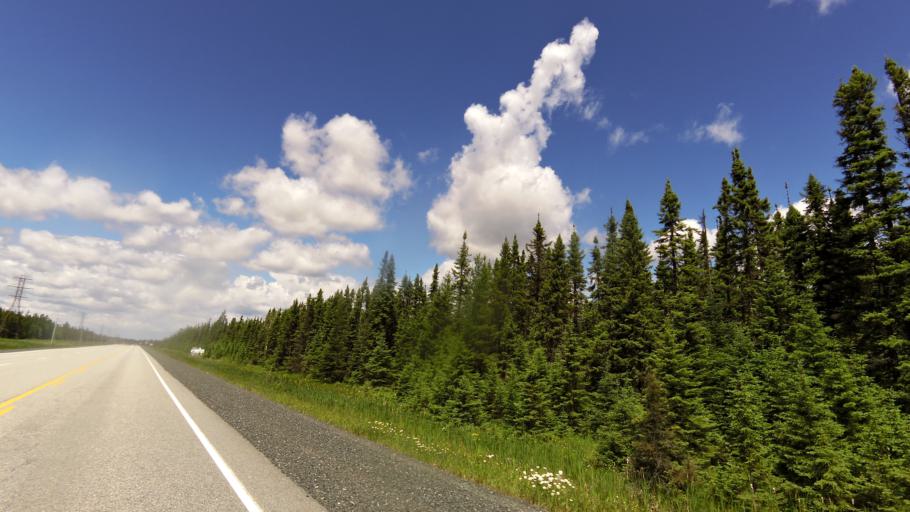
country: CA
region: Ontario
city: Timmins
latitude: 49.2600
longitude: -81.5862
